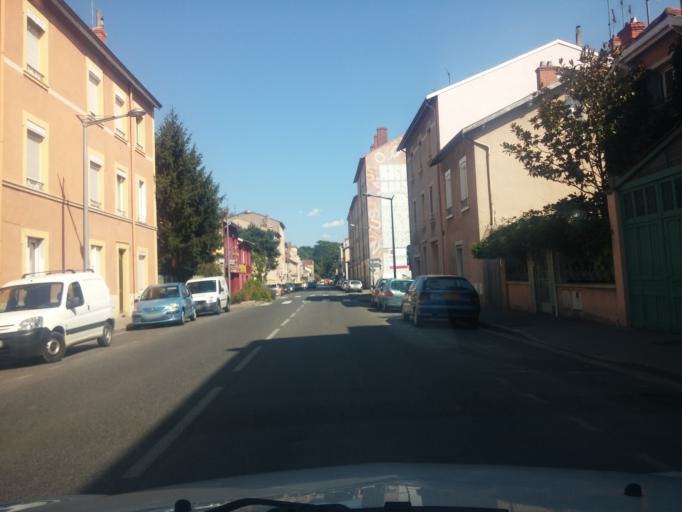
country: FR
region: Rhone-Alpes
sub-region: Departement du Rhone
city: Oullins
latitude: 45.7198
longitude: 4.7997
